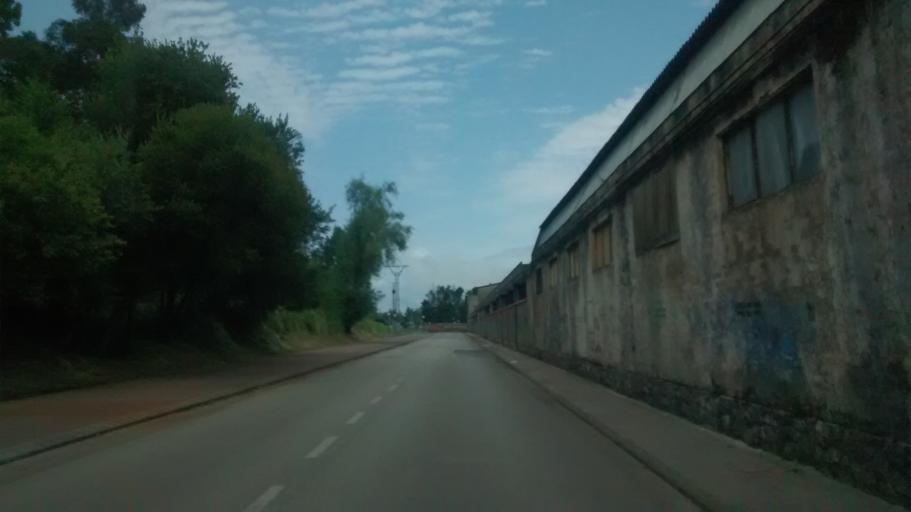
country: ES
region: Cantabria
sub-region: Provincia de Cantabria
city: El Astillero
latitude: 43.4193
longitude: -3.8129
